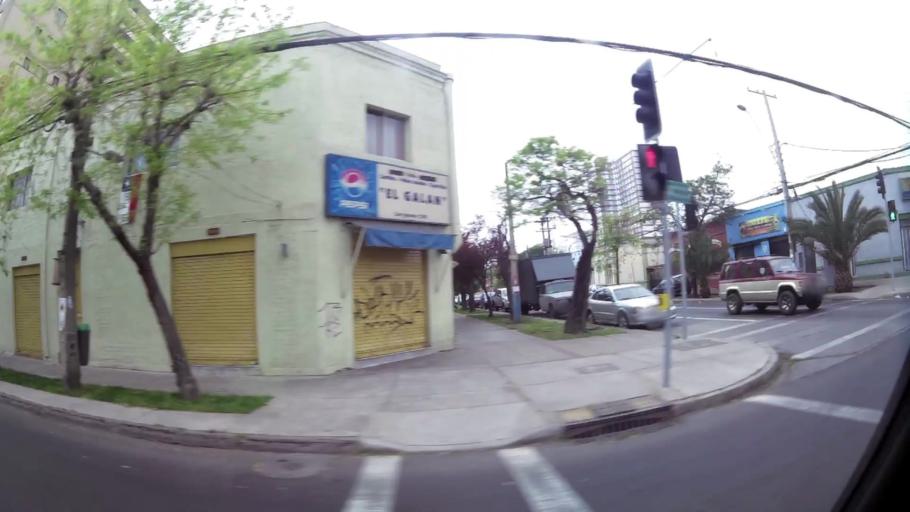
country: CL
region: Santiago Metropolitan
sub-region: Provincia de Santiago
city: Santiago
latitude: -33.4646
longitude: -70.6550
